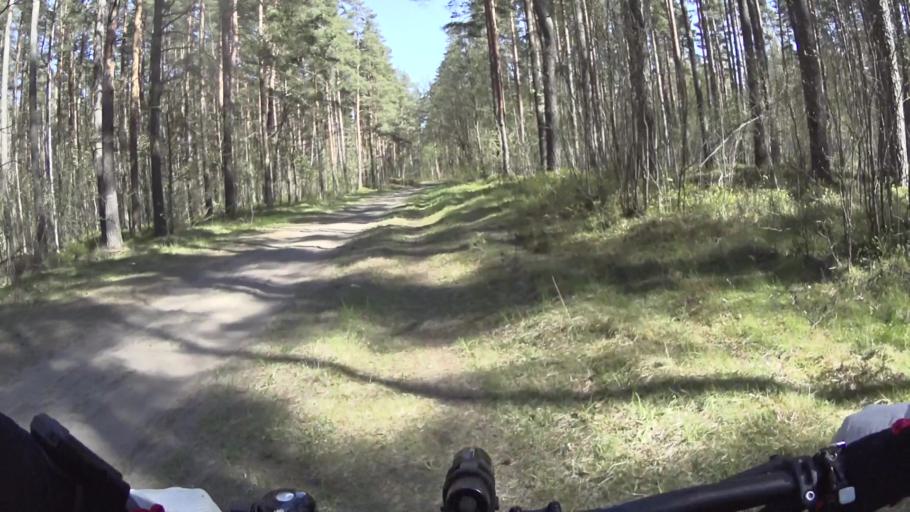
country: LV
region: Riga
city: Bolderaja
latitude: 56.9808
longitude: 24.0122
